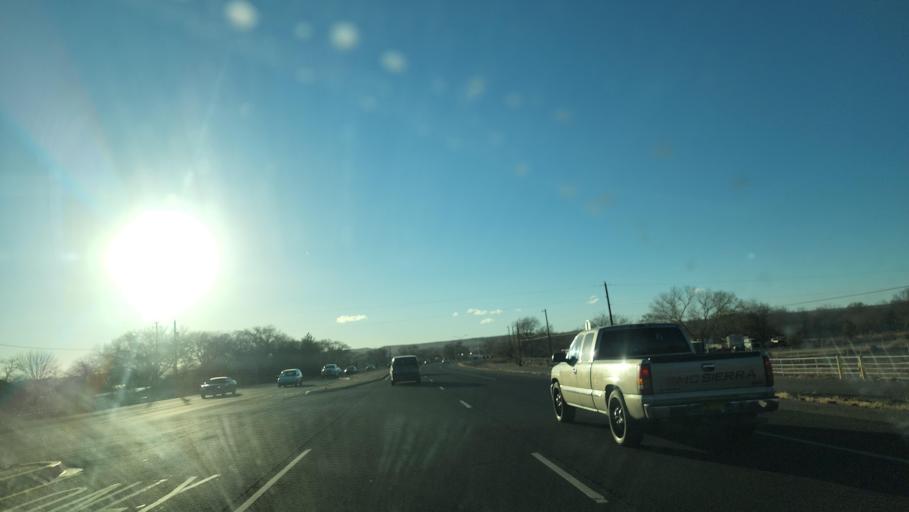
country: US
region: New Mexico
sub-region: Bernalillo County
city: South Valley
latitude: 35.0266
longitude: -106.7029
